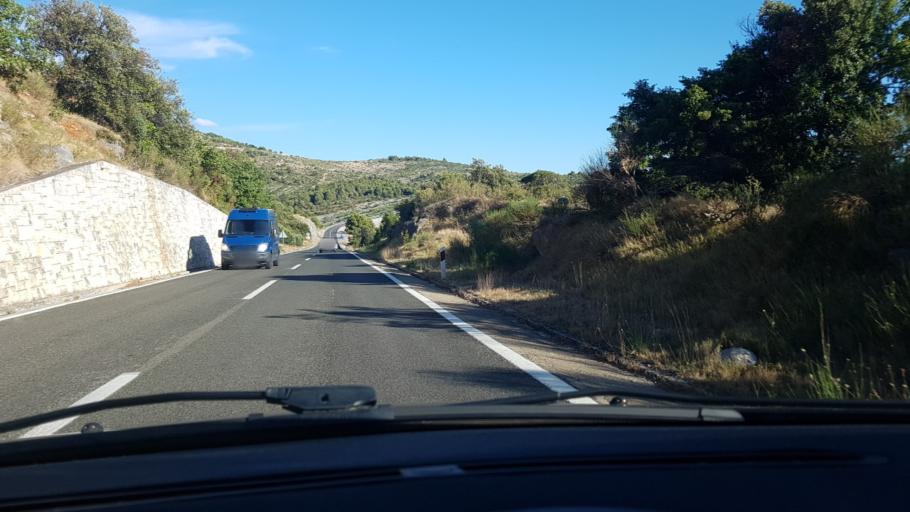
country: HR
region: Sibensko-Kniniska
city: Primosten
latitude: 43.5723
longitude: 15.9428
